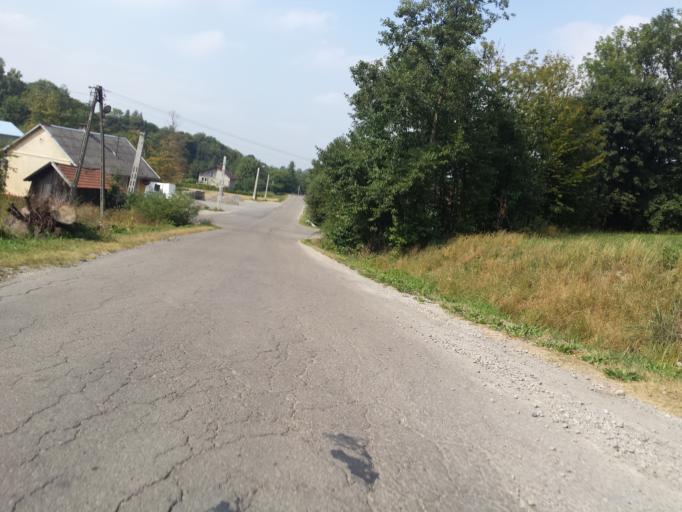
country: PL
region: Subcarpathian Voivodeship
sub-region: Powiat rzeszowski
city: Blazowa
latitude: 49.8479
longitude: 22.1423
